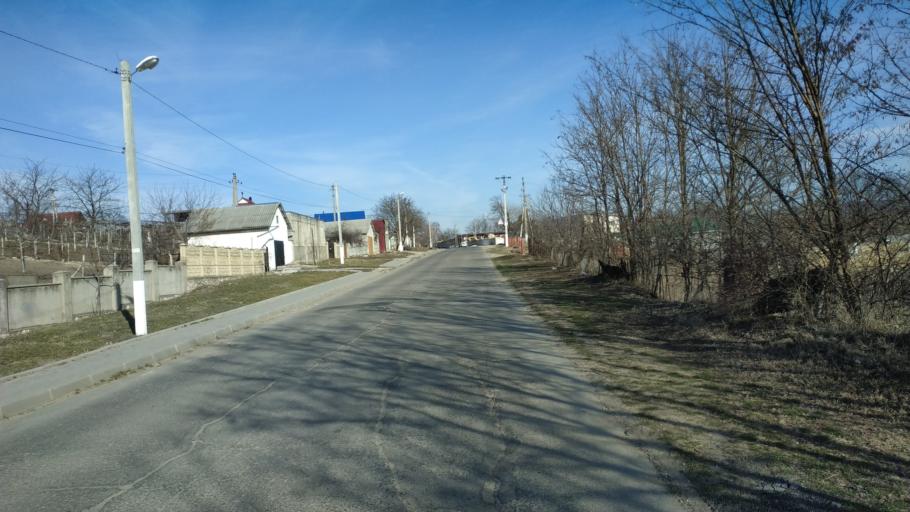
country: MD
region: Chisinau
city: Vatra
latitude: 47.0024
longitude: 28.6720
